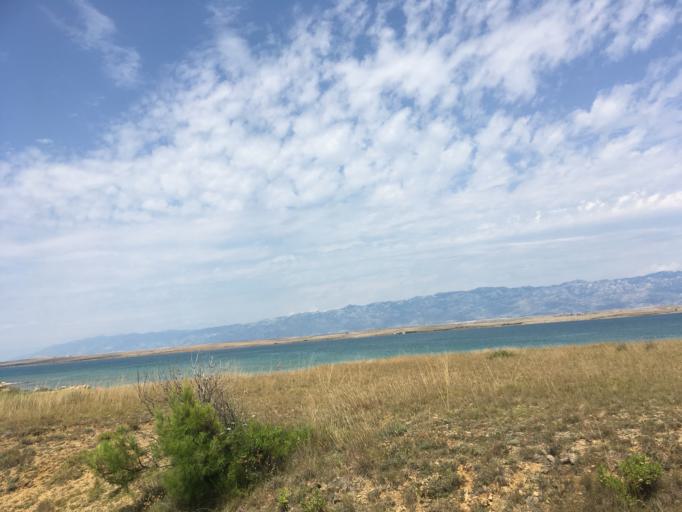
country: HR
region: Zadarska
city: Privlaka
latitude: 44.2734
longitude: 15.1479
